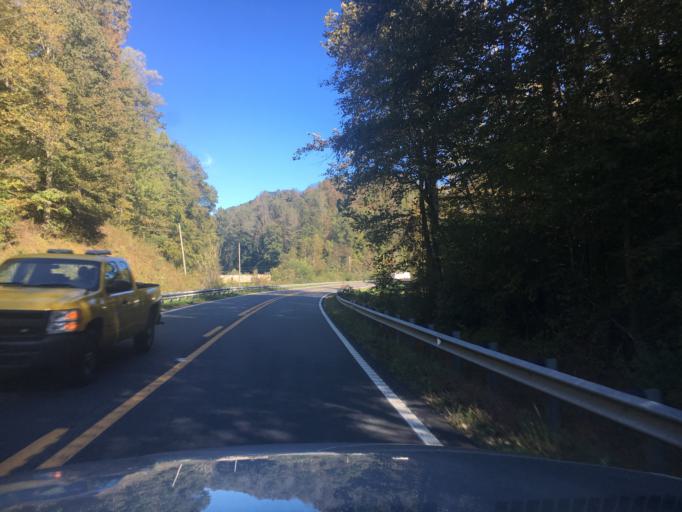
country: US
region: North Carolina
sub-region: Burke County
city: Glen Alpine
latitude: 35.5674
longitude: -81.8508
